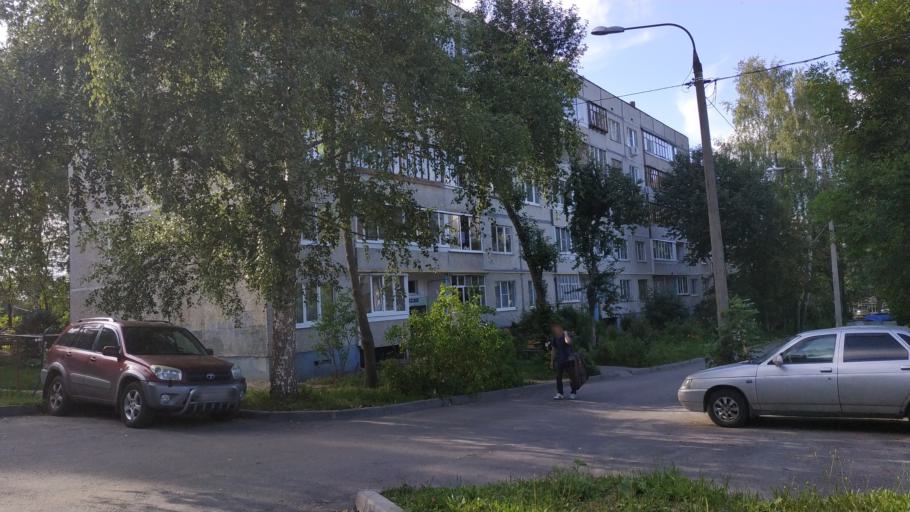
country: RU
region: Chuvashia
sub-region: Cheboksarskiy Rayon
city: Cheboksary
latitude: 56.1441
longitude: 47.1828
